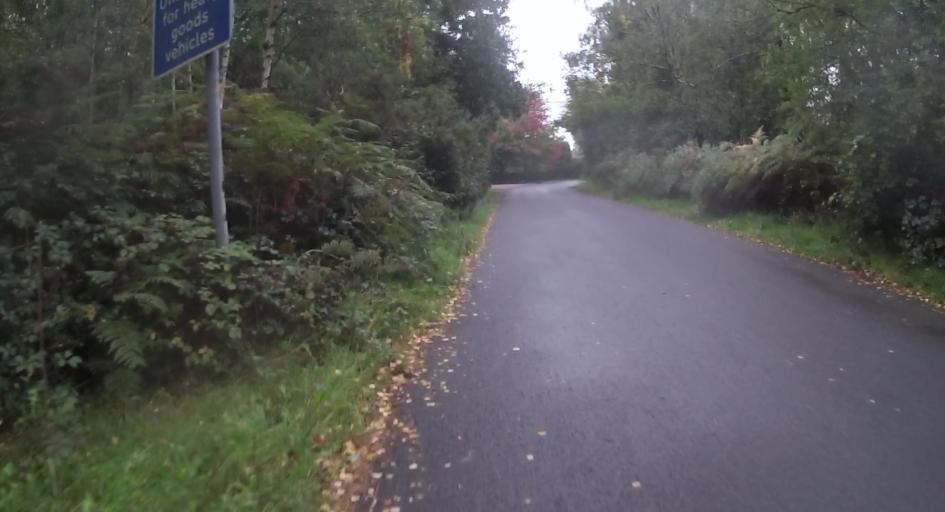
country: GB
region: England
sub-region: West Berkshire
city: Thatcham
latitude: 51.4143
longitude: -1.2140
